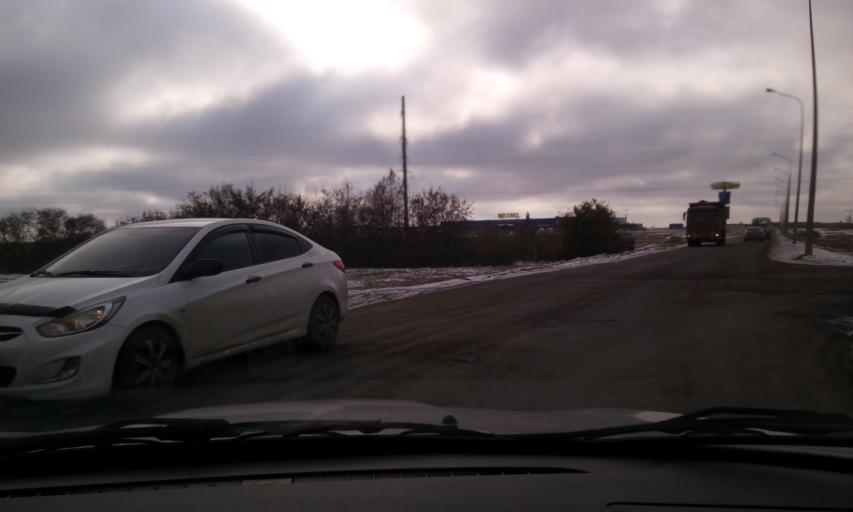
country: KZ
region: Astana Qalasy
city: Astana
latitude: 51.1357
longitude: 71.5452
